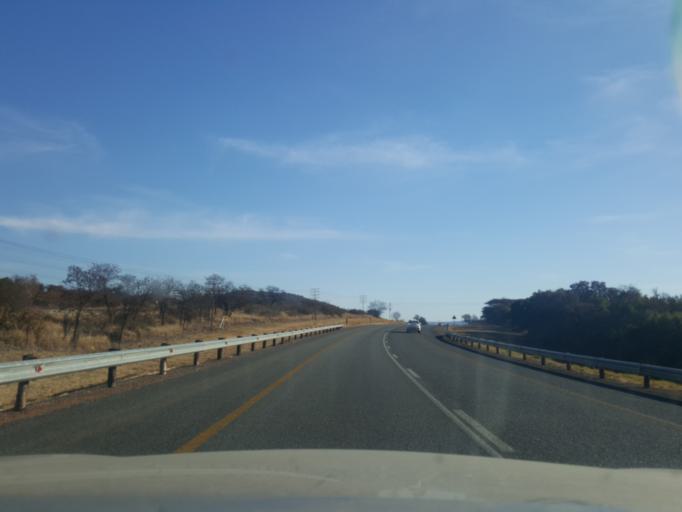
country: ZA
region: North-West
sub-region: Ngaka Modiri Molema District Municipality
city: Zeerust
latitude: -25.5364
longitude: 26.1296
